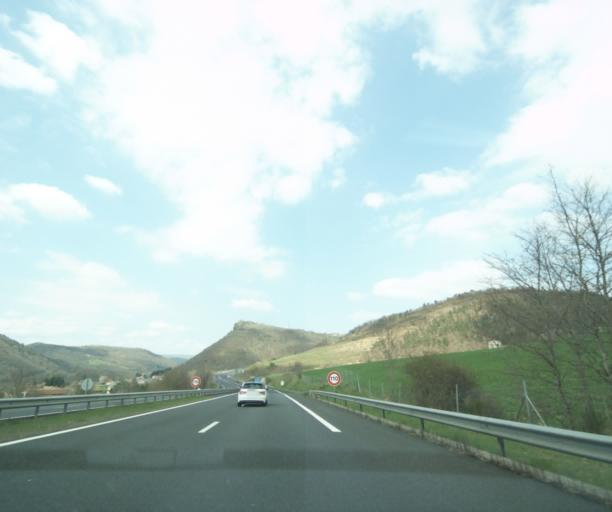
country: FR
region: Auvergne
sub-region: Departement du Cantal
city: Massiac
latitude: 45.2601
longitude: 3.2022
